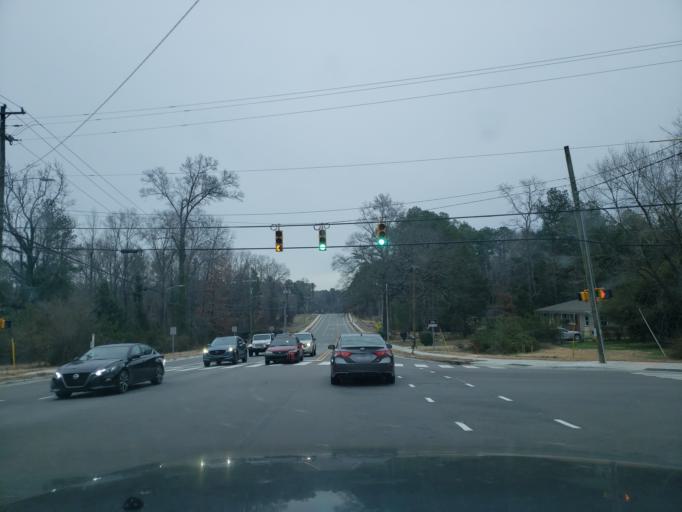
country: US
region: North Carolina
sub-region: Orange County
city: Chapel Hill
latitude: 35.9433
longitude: -78.9832
